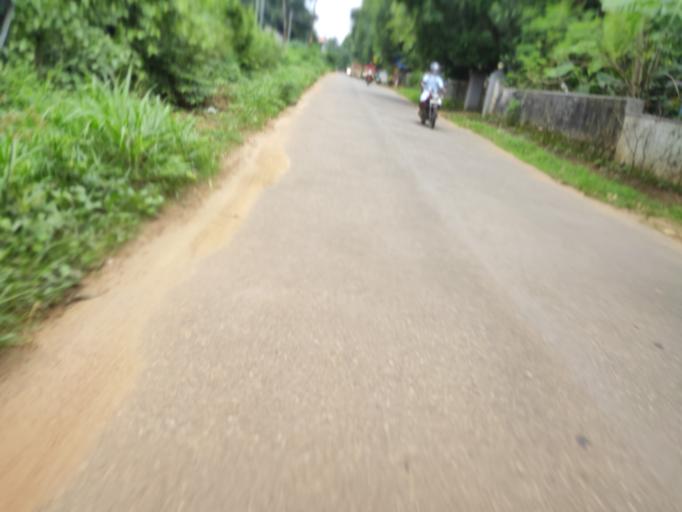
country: IN
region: Kerala
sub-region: Malappuram
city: Manjeri
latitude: 11.2351
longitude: 76.2851
